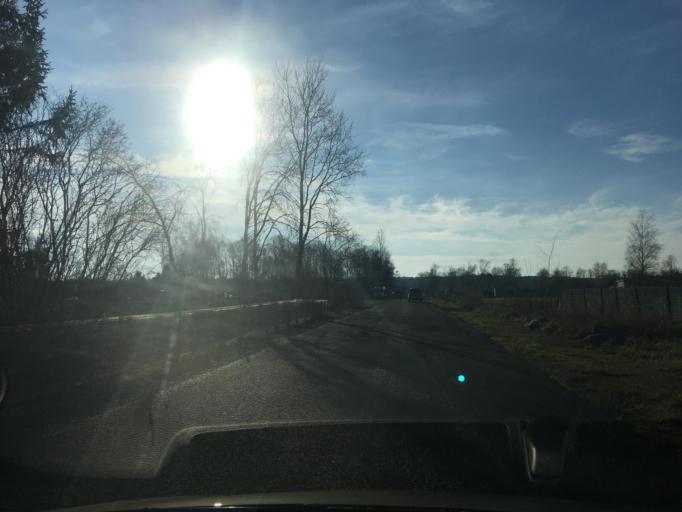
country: EE
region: Harju
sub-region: Maardu linn
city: Maardu
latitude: 59.4800
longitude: 25.0483
